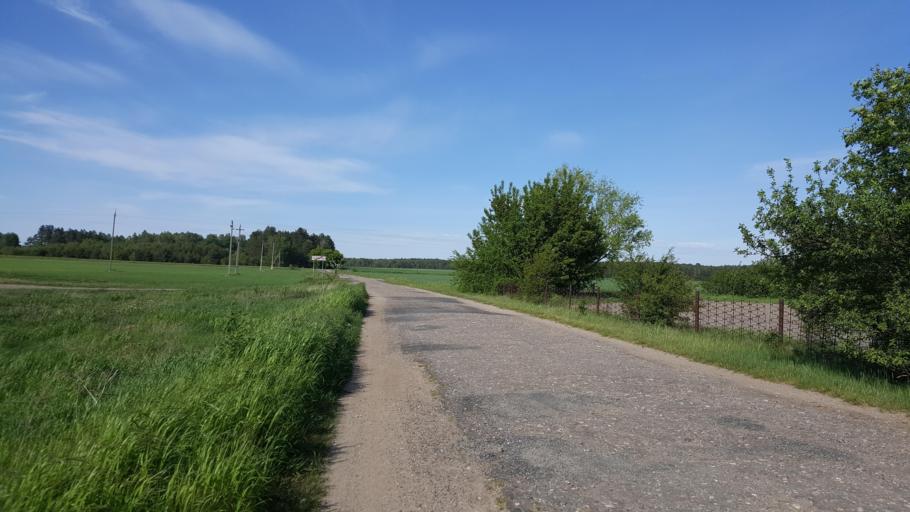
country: BY
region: Brest
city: Zhabinka
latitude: 52.3166
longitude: 23.9447
